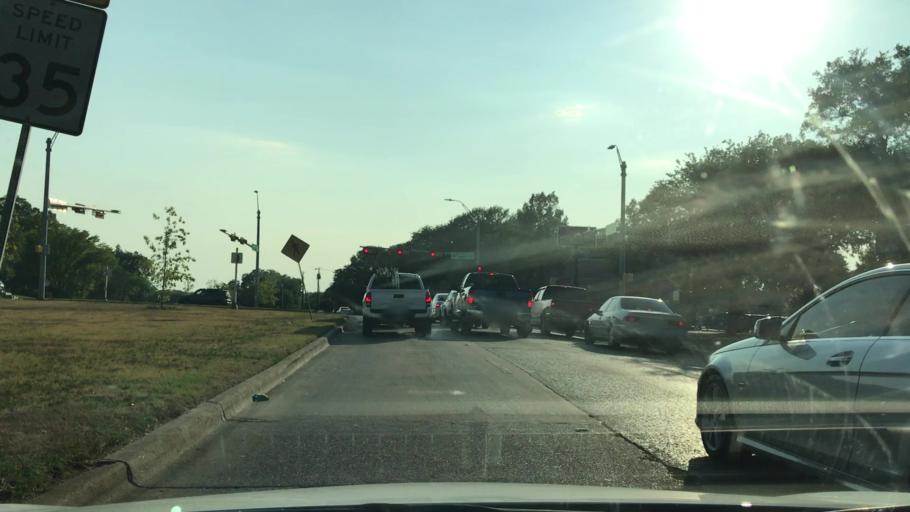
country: US
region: Texas
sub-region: Dallas County
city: Cockrell Hill
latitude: 32.7480
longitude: -96.8619
